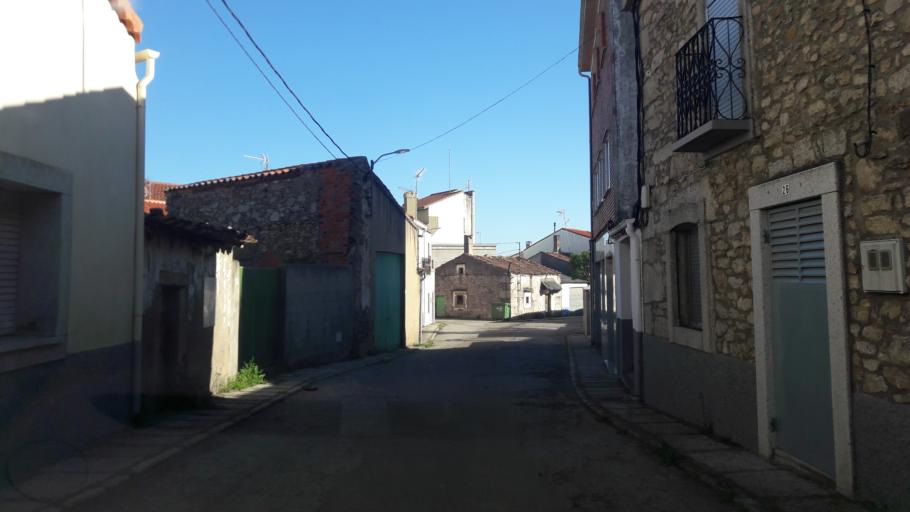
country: ES
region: Castille and Leon
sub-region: Provincia de Salamanca
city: Villavieja de Yeltes
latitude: 40.8770
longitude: -6.4673
